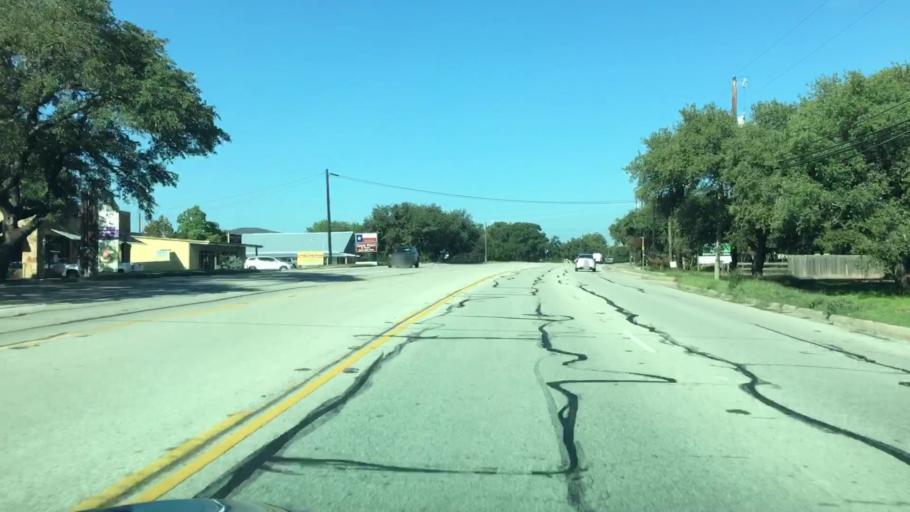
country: US
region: Texas
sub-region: Hays County
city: Dripping Springs
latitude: 30.1924
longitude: -98.0975
